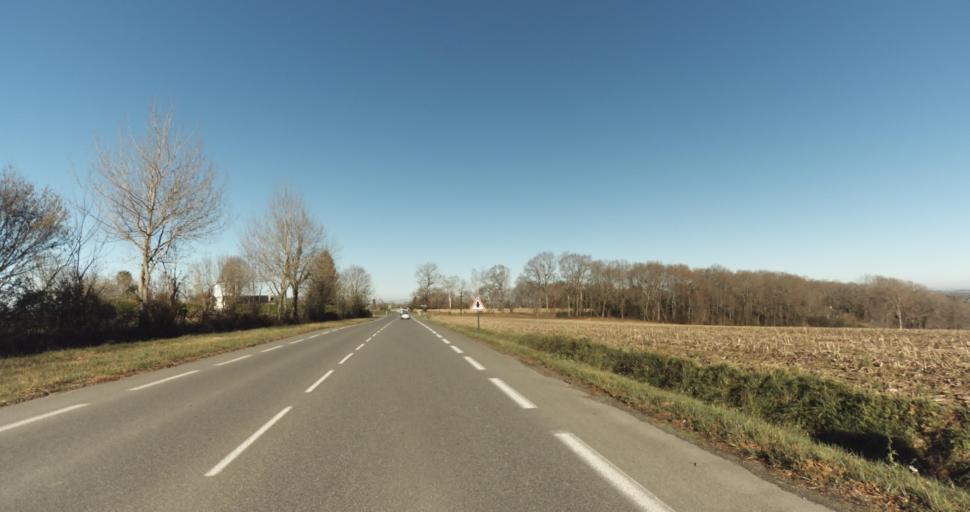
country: FR
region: Aquitaine
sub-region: Departement des Pyrenees-Atlantiques
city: Morlaas
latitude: 43.3421
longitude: -0.2757
